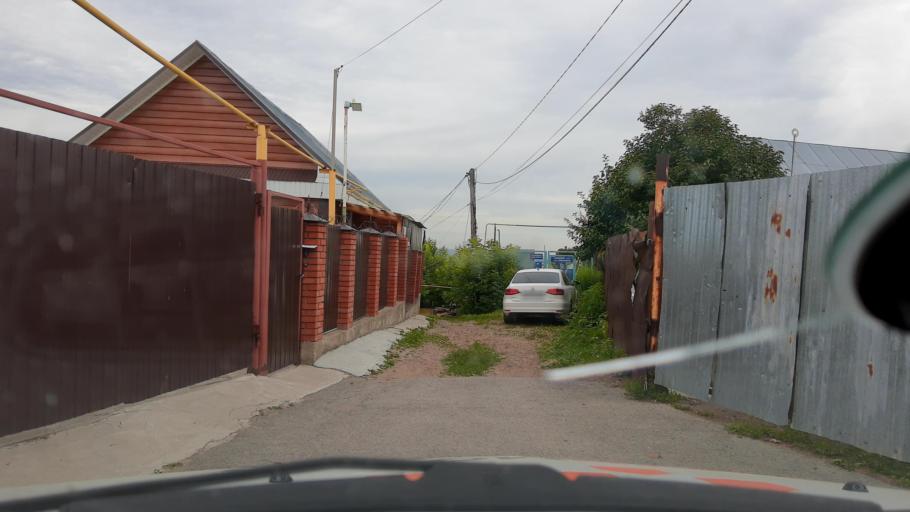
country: RU
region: Bashkortostan
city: Ufa
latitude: 54.7439
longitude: 55.9448
